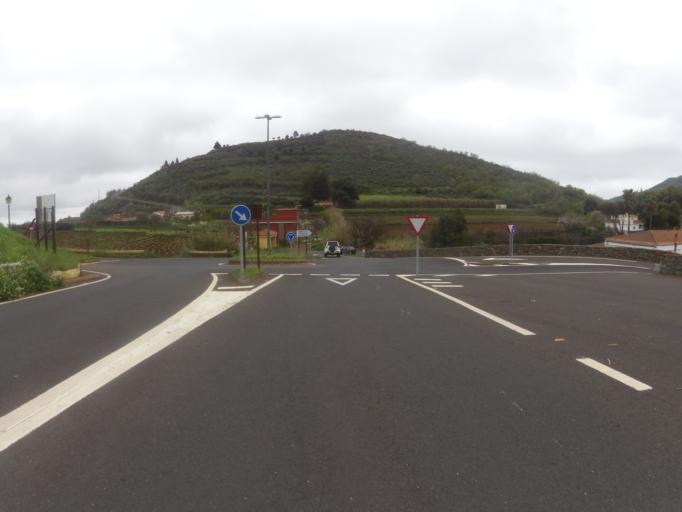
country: ES
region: Canary Islands
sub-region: Provincia de Las Palmas
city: Vega de San Mateo
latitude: 28.0090
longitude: -15.5442
